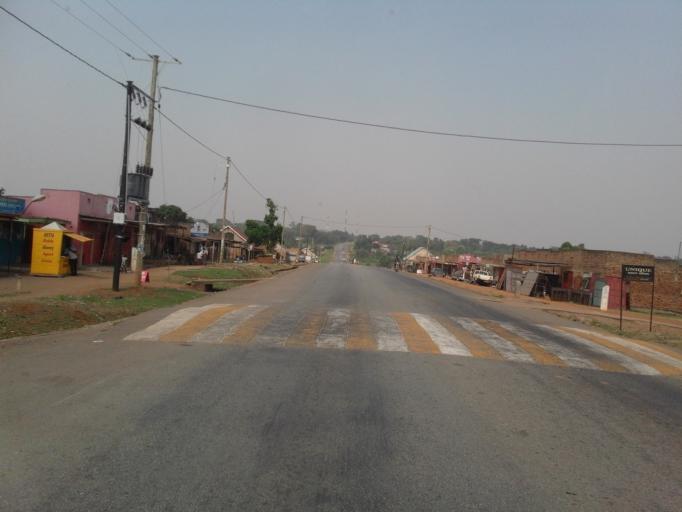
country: UG
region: Eastern Region
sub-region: Bugiri District
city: Bugiri
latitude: 0.6234
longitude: 33.6200
